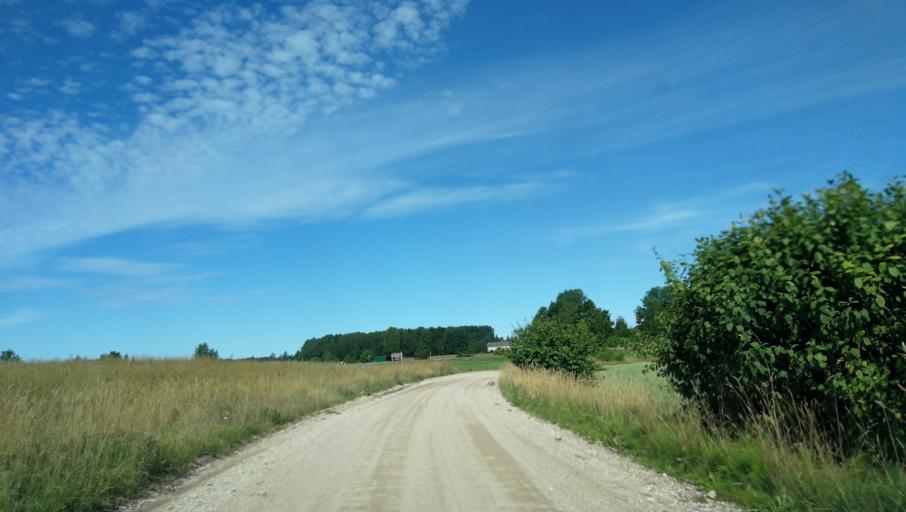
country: LV
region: Gulbenes Rajons
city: Gulbene
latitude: 57.1840
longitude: 26.8629
